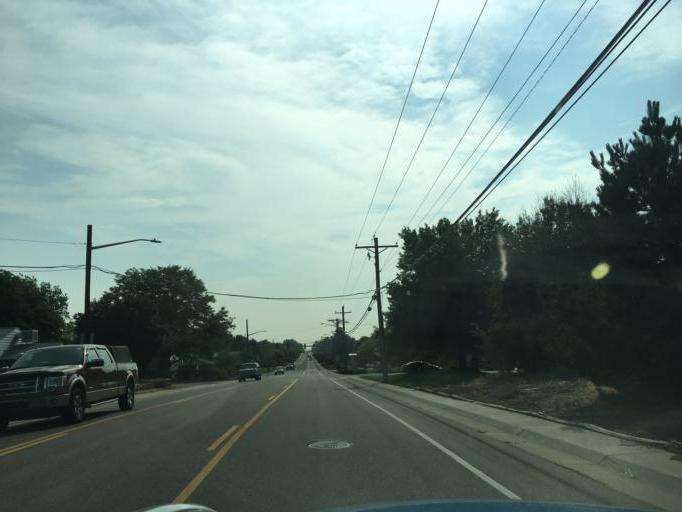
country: US
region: Colorado
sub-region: Jefferson County
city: Arvada
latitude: 39.8128
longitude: -105.0693
